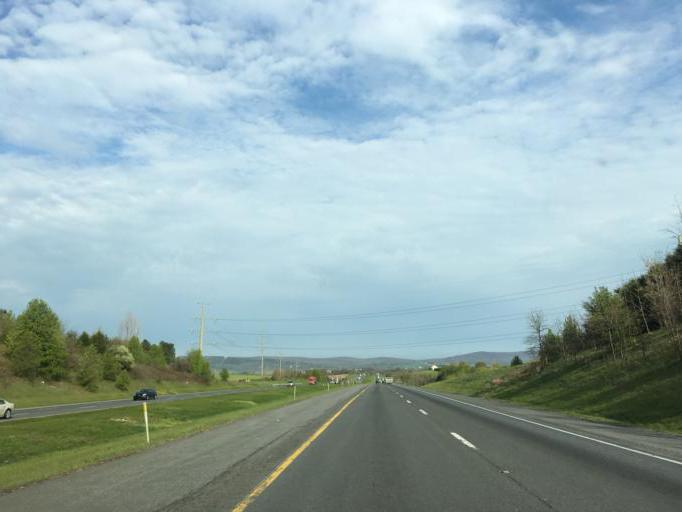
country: US
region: Maryland
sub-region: Frederick County
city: Middletown
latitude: 39.4642
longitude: -77.5167
